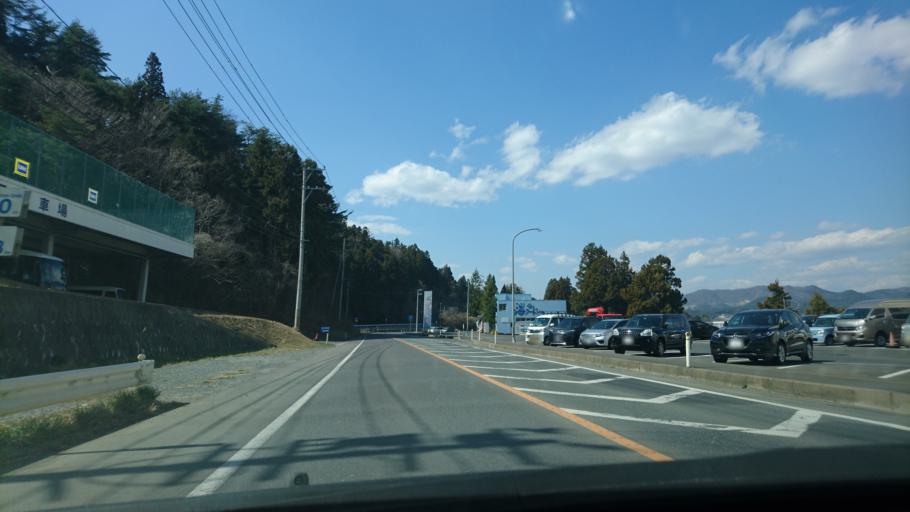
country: JP
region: Miyagi
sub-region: Oshika Gun
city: Onagawa Cho
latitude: 38.6587
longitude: 141.4482
